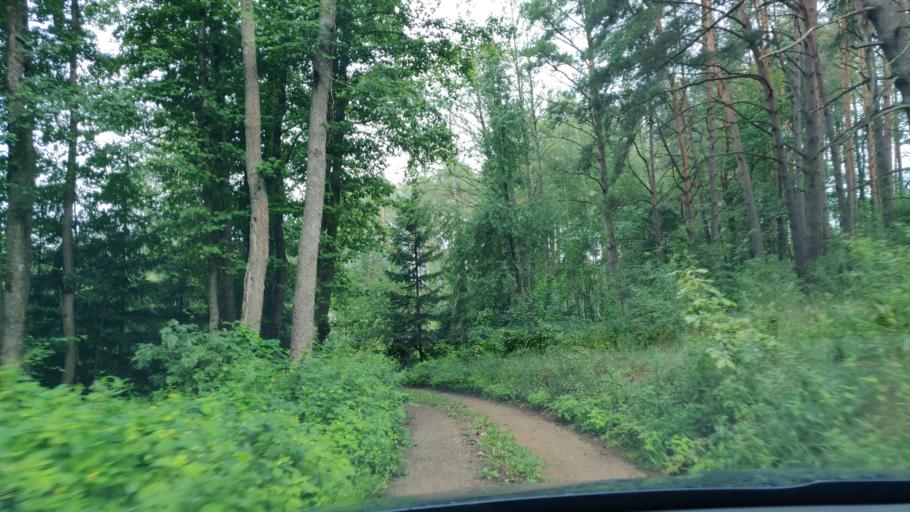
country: LT
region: Vilnius County
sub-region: Trakai
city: Rudiskes
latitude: 54.6102
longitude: 24.8237
